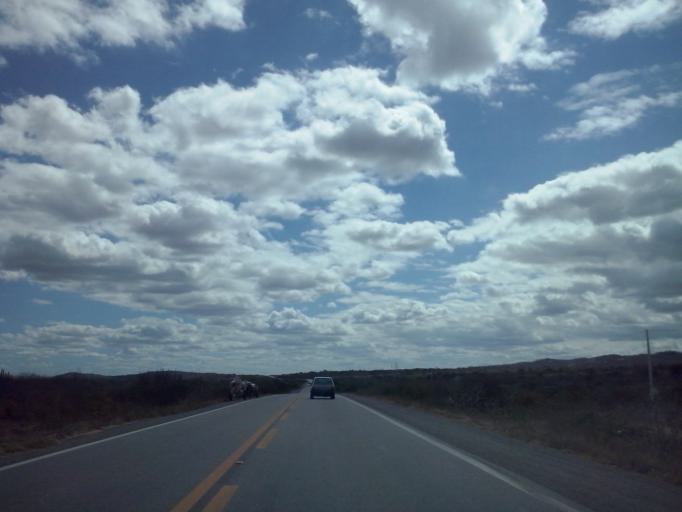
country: BR
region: Paraiba
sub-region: Soledade
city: Soledade
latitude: -7.0480
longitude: -36.3871
